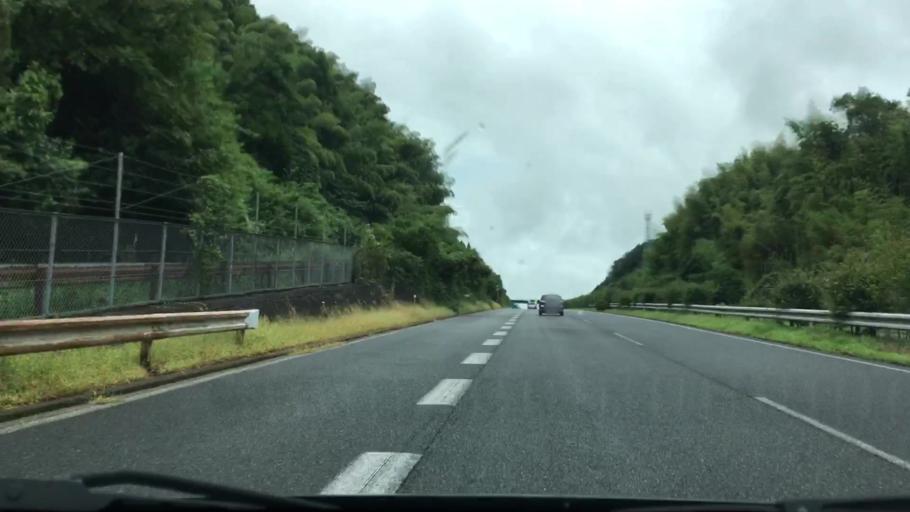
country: JP
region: Hyogo
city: Yamazakicho-nakabirose
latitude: 34.9743
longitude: 134.6501
